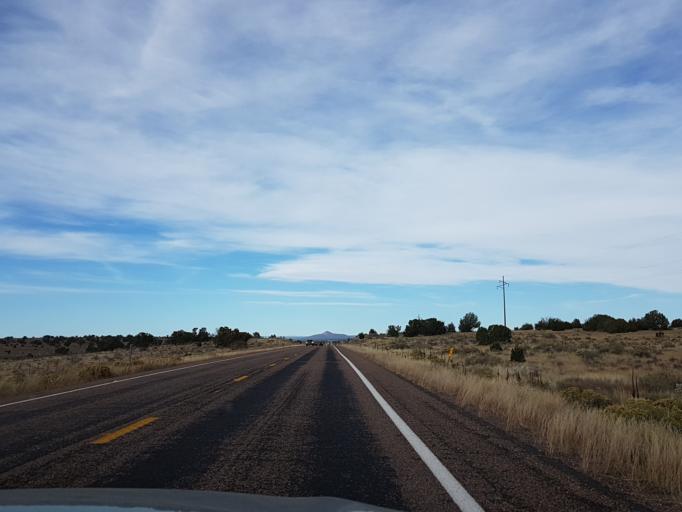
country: US
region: Arizona
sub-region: Coconino County
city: Williams
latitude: 35.5610
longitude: -112.1576
